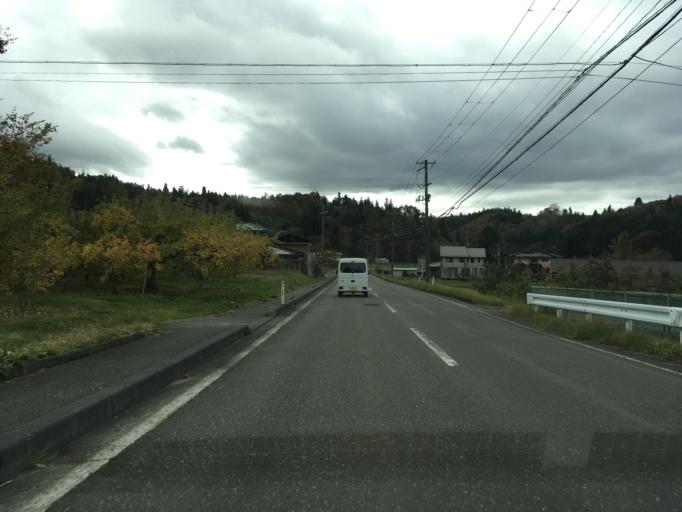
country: JP
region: Iwate
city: Mizusawa
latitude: 39.0625
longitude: 141.3609
